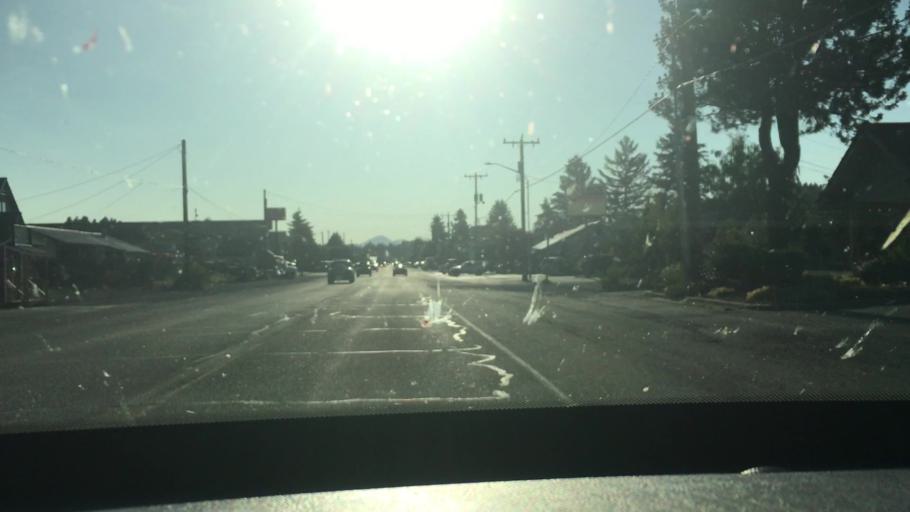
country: US
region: Washington
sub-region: Kittitas County
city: Cle Elum
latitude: 47.1924
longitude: -120.9182
